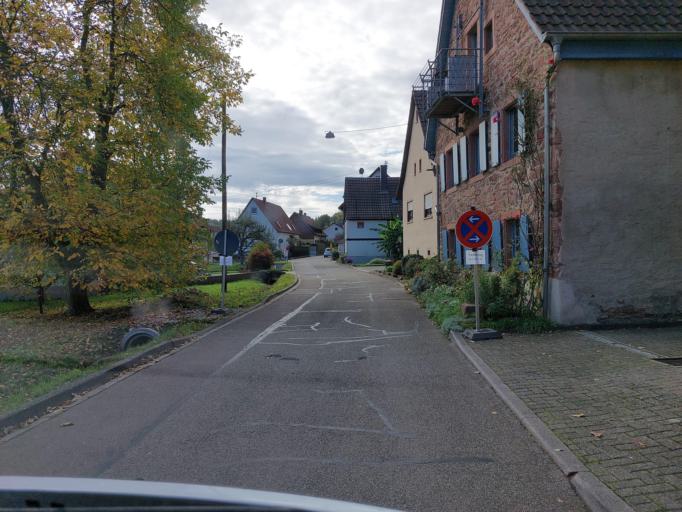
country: DE
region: Baden-Wuerttemberg
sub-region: Freiburg Region
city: Malterdingen
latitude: 48.1634
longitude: 7.8285
